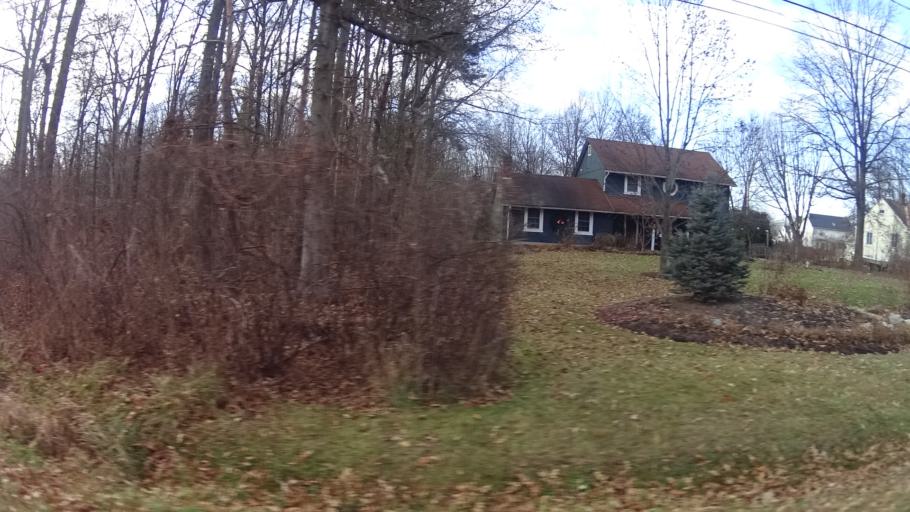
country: US
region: Ohio
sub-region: Lorain County
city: North Ridgeville
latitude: 41.3555
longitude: -81.9915
